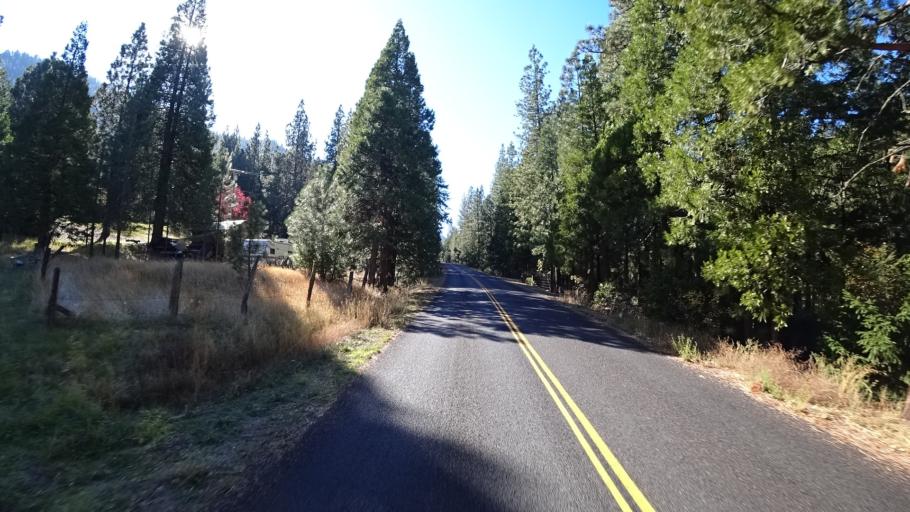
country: US
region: California
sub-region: Siskiyou County
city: Weed
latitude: 41.4236
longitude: -122.5004
